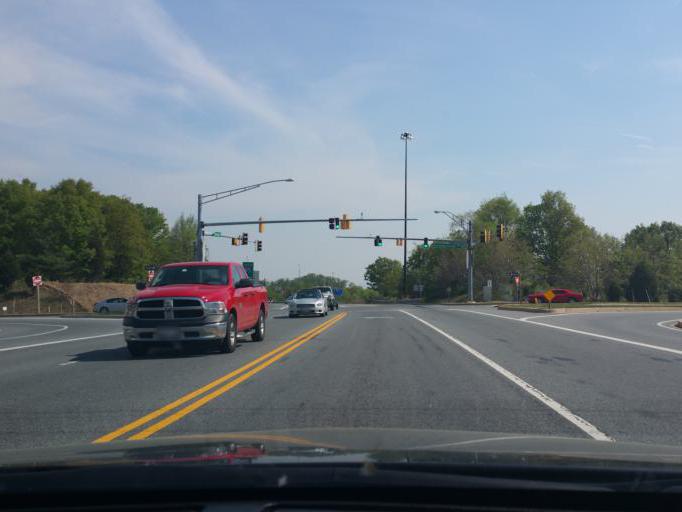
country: US
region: Maryland
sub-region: Cecil County
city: Perryville
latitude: 39.5964
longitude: -76.0677
